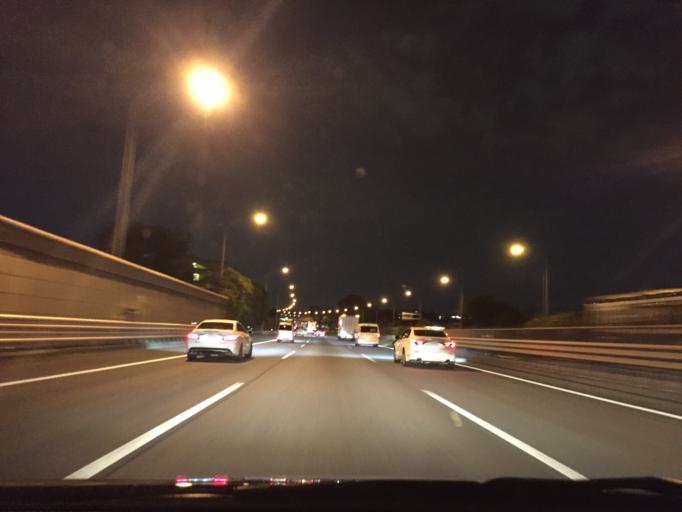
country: JP
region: Tokyo
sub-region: Machida-shi
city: Machida
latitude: 35.5294
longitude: 139.5174
